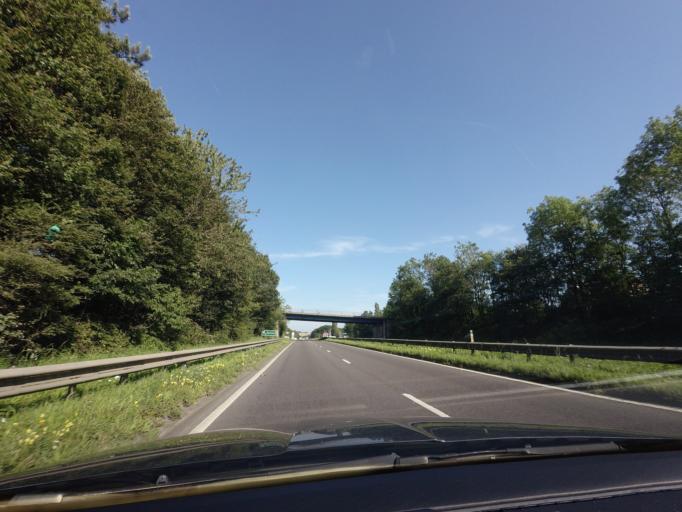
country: GB
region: England
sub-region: Derbyshire
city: Pilsley
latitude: 53.2008
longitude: -1.3444
